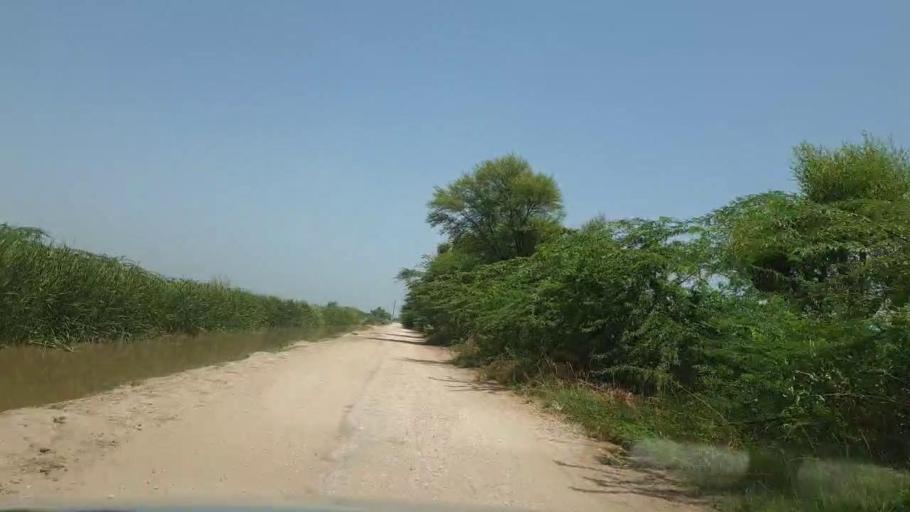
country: PK
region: Sindh
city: Rohri
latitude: 27.6355
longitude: 69.1010
